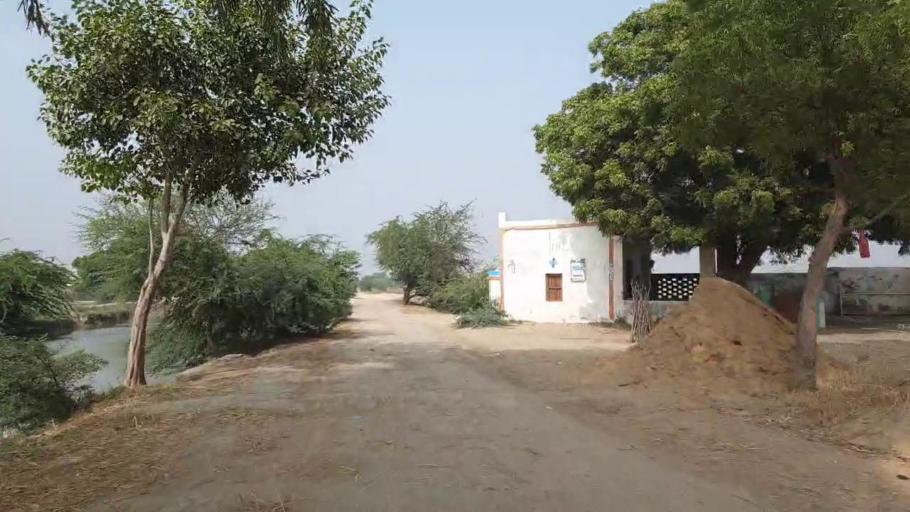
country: PK
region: Sindh
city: Kario
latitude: 24.8778
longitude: 68.5141
